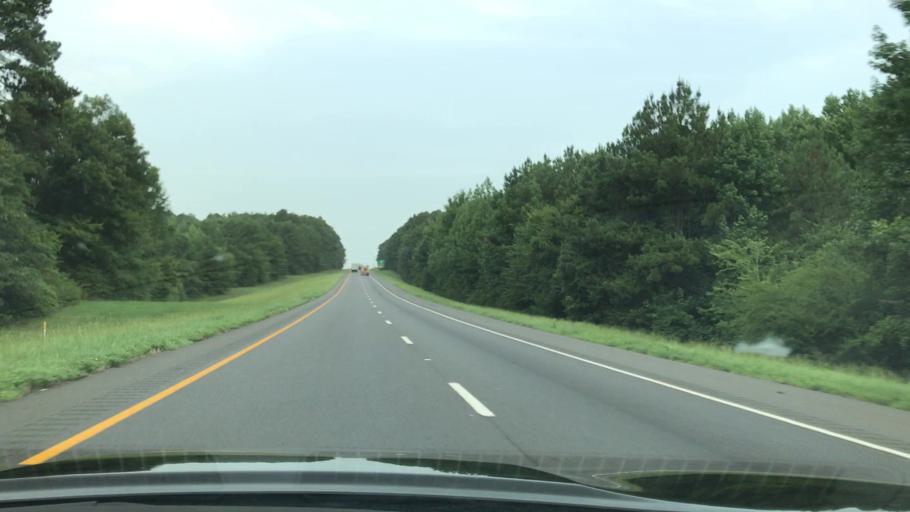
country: US
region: Texas
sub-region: Harrison County
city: Marshall
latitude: 32.4896
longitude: -94.3978
